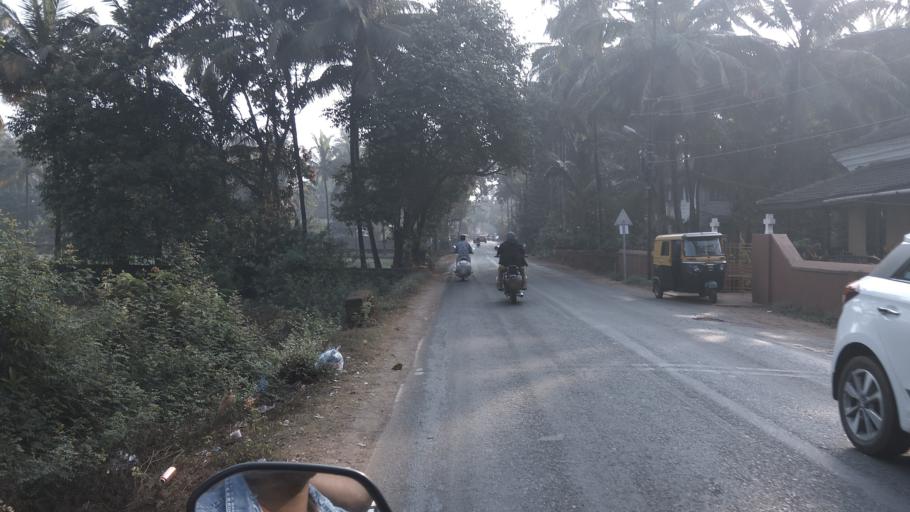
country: IN
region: Goa
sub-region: North Goa
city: Saligao
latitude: 15.5462
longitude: 73.7937
